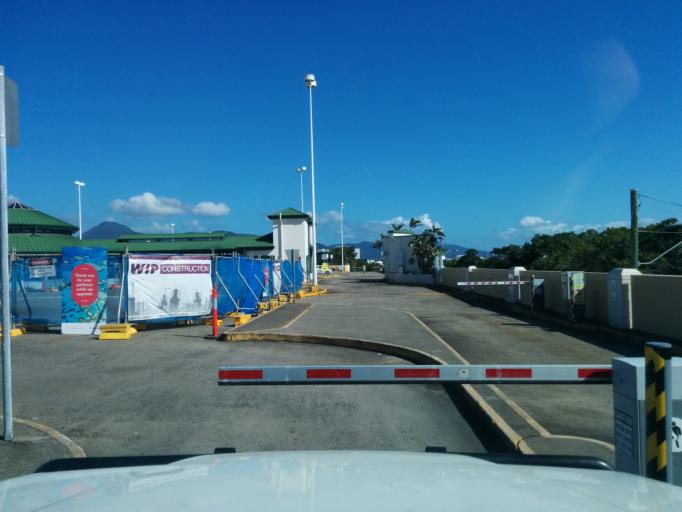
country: AU
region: Queensland
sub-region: Cairns
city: Cairns
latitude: -16.9258
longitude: 145.7714
